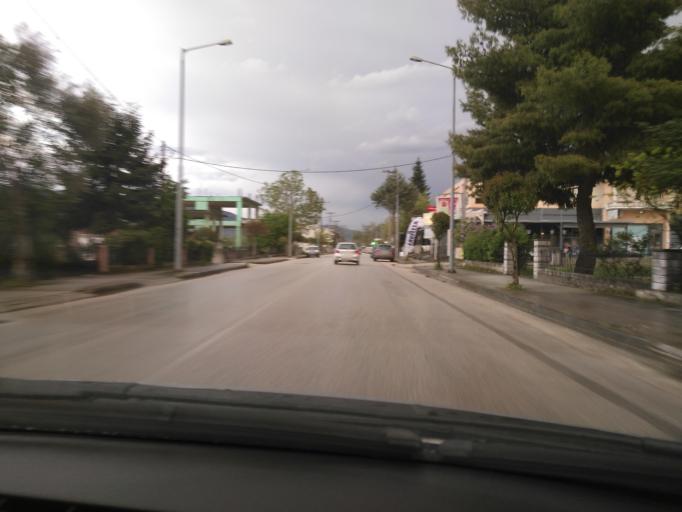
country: GR
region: Epirus
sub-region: Nomos Ioanninon
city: Katsikas
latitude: 39.6258
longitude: 20.8844
